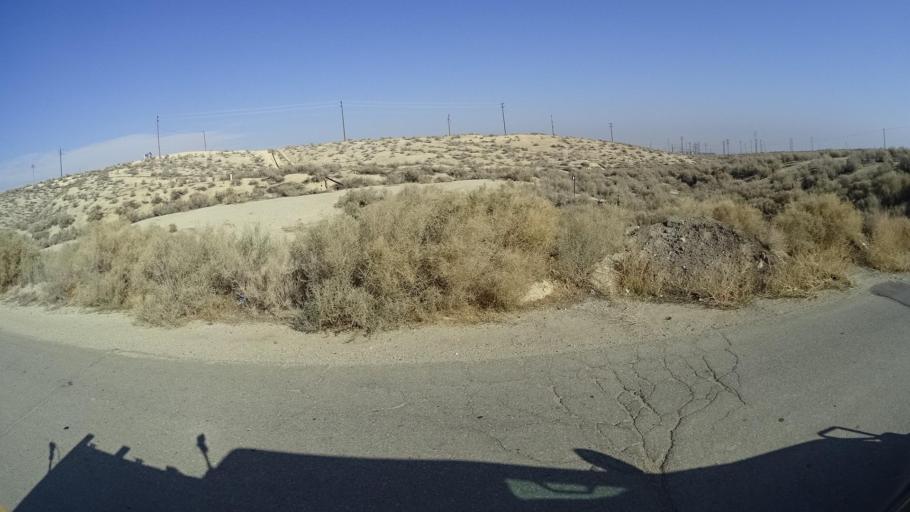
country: US
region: California
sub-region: Kern County
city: Taft Heights
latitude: 35.1432
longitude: -119.5073
